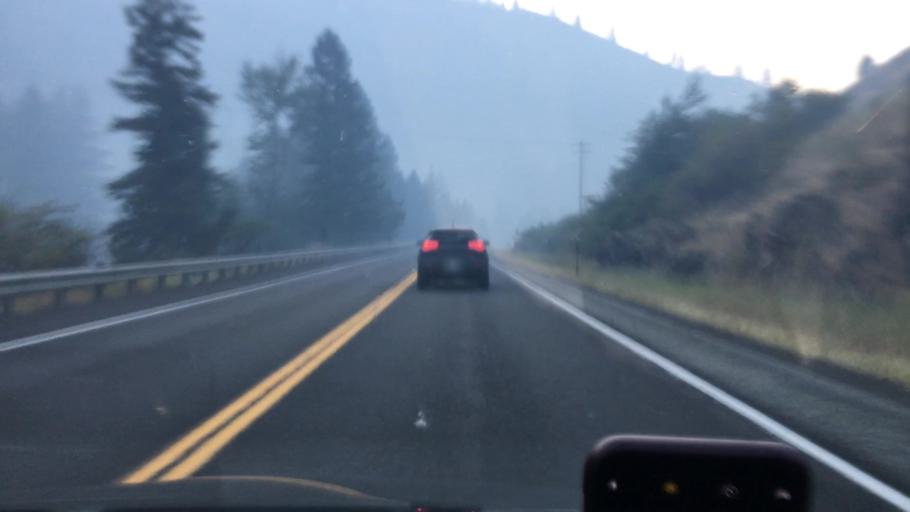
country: US
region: Idaho
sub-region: Valley County
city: McCall
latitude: 45.2689
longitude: -116.3435
